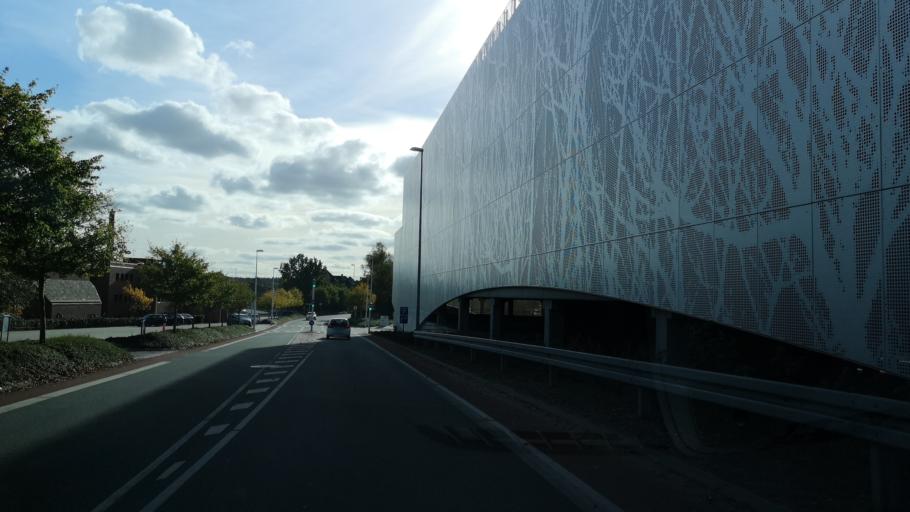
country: DK
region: Central Jutland
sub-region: Holstebro Kommune
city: Holstebro
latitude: 56.3610
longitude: 8.6152
